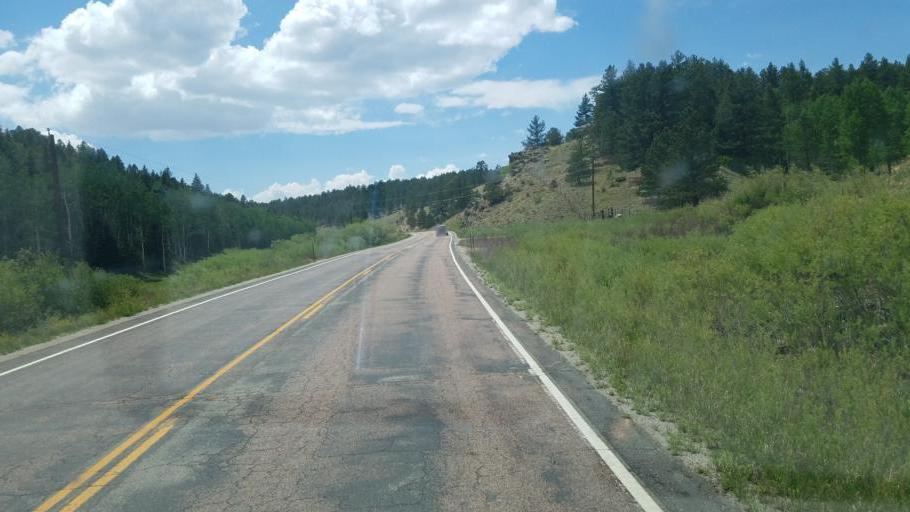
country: US
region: Colorado
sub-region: Fremont County
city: Florence
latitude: 38.1663
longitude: -105.2112
